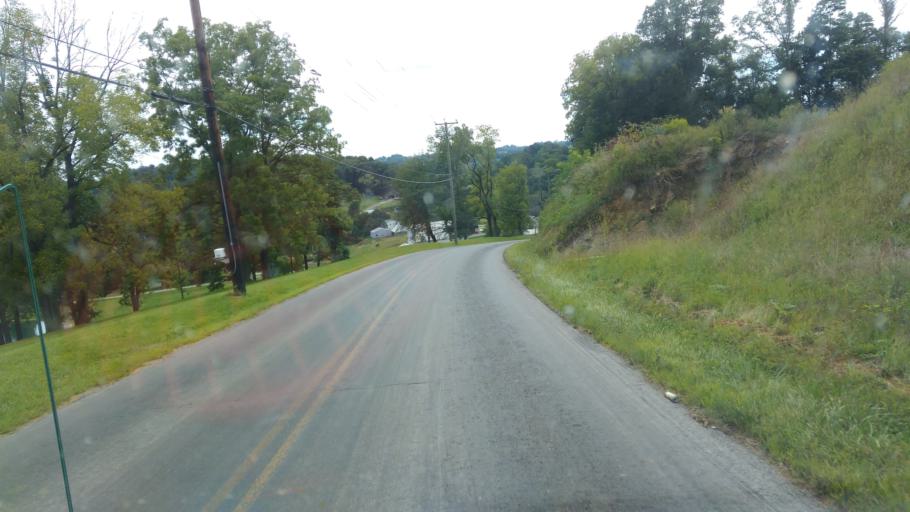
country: US
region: Ohio
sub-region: Holmes County
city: Millersburg
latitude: 40.5451
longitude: -81.8034
